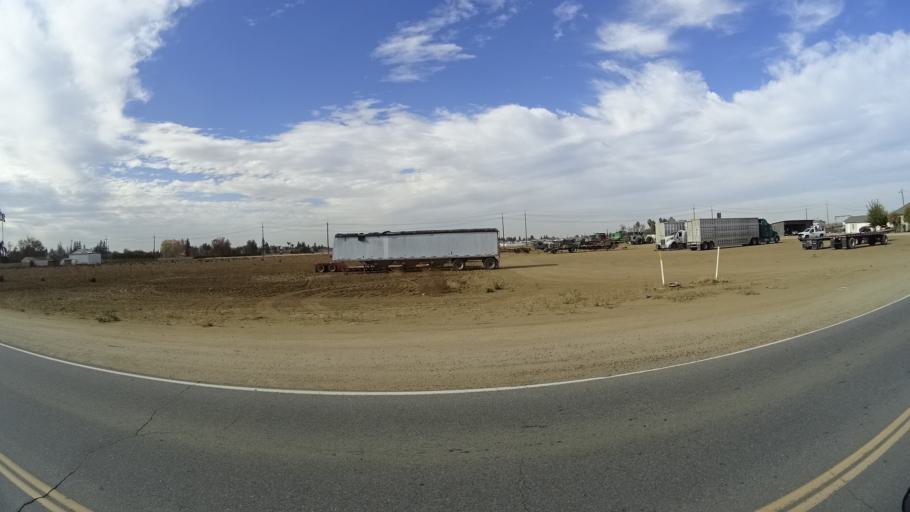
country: US
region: California
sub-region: Kern County
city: Greenacres
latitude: 35.4249
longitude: -119.0920
